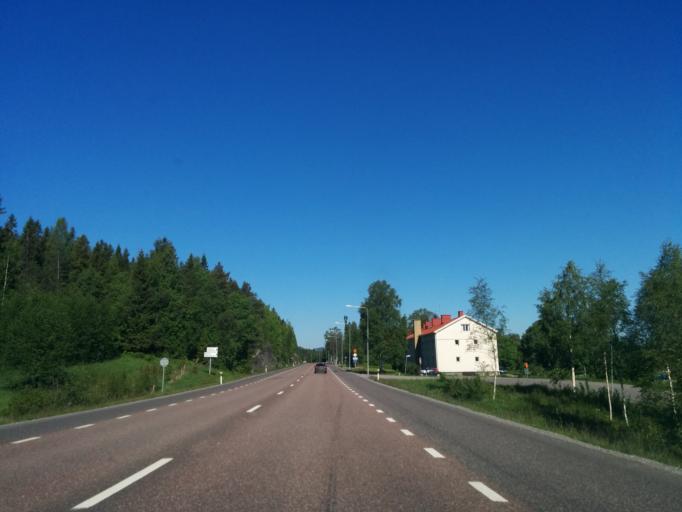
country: SE
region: Vaesternorrland
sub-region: Kramfors Kommun
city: Kramfors
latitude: 62.9072
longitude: 17.8202
